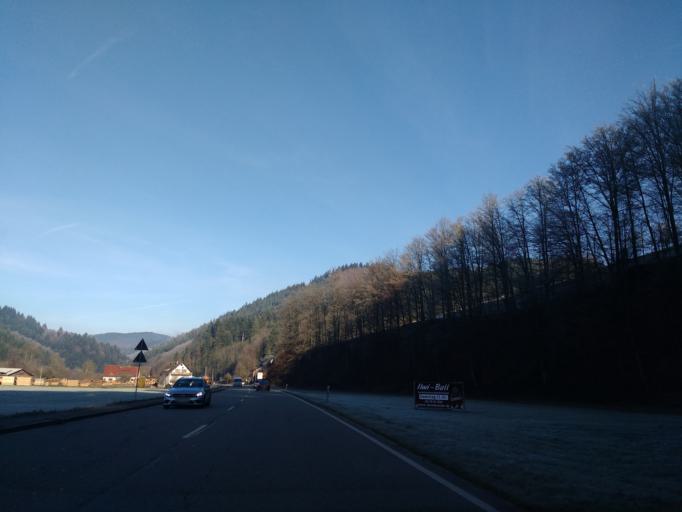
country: DE
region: Baden-Wuerttemberg
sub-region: Freiburg Region
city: Oppenau
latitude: 48.4935
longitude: 8.1420
